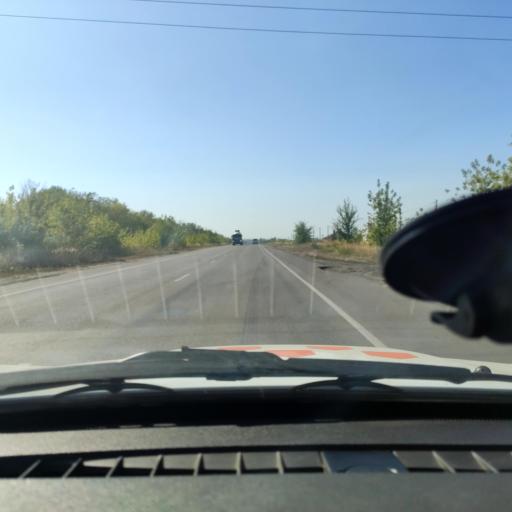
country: RU
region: Voronezj
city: Novaya Usman'
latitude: 51.6171
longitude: 39.3360
